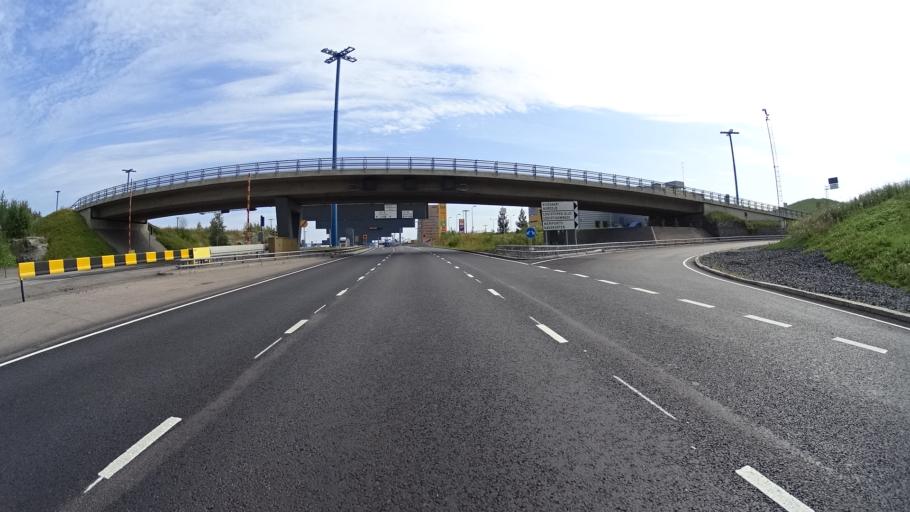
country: FI
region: Uusimaa
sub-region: Helsinki
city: Vantaa
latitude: 60.2262
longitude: 25.1674
